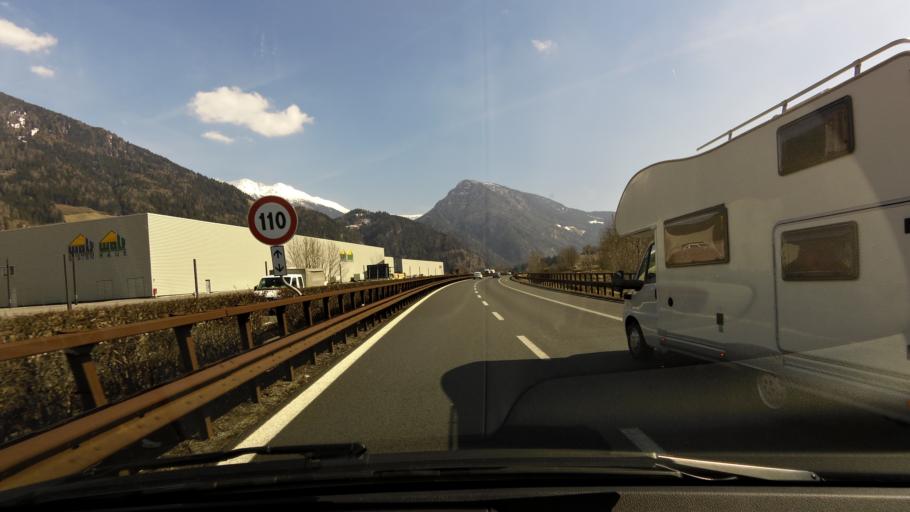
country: IT
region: Trentino-Alto Adige
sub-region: Bolzano
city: Campo di Trens
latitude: 46.8666
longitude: 11.4904
